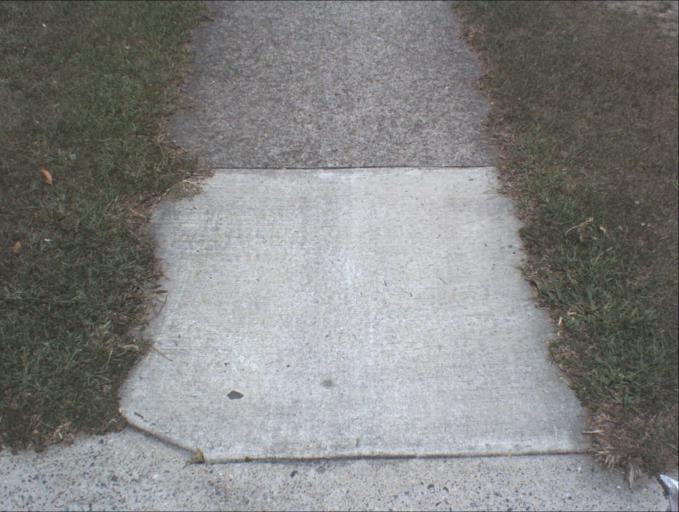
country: AU
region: Queensland
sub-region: Logan
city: Slacks Creek
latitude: -27.6714
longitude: 153.1472
